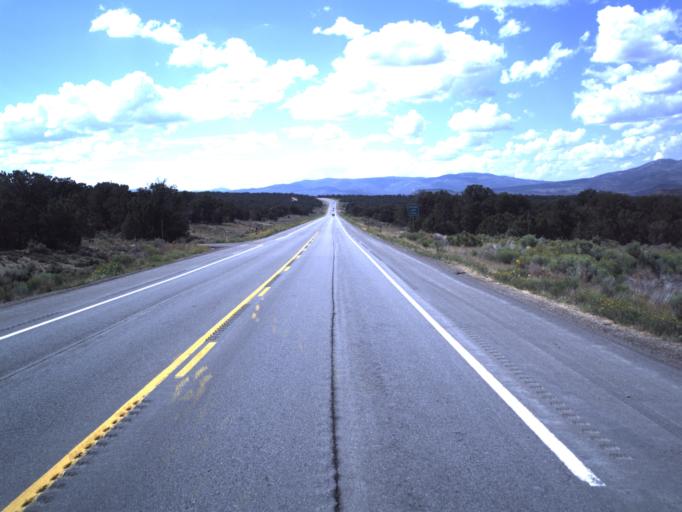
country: US
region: Utah
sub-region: Duchesne County
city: Duchesne
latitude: 40.1895
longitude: -110.6763
